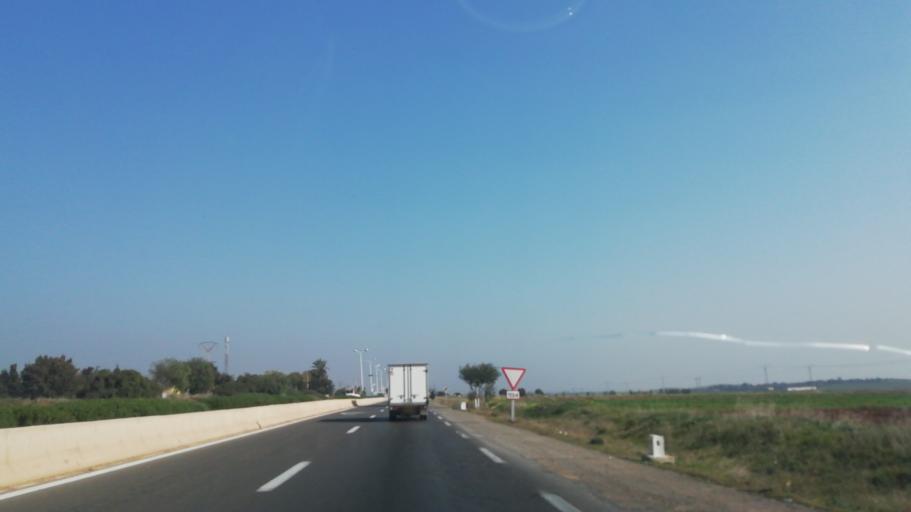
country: DZ
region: Ain Temouchent
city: El Amria
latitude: 35.5448
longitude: -0.9667
